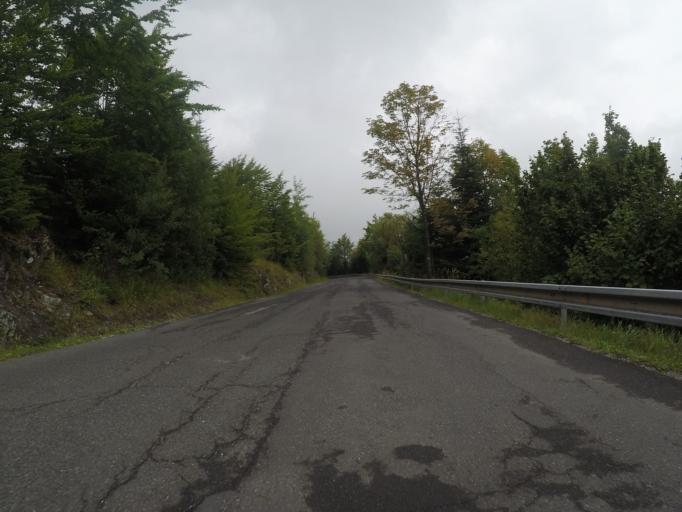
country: SK
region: Kosicky
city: Spisska Nova Ves
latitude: 48.8686
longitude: 20.5265
